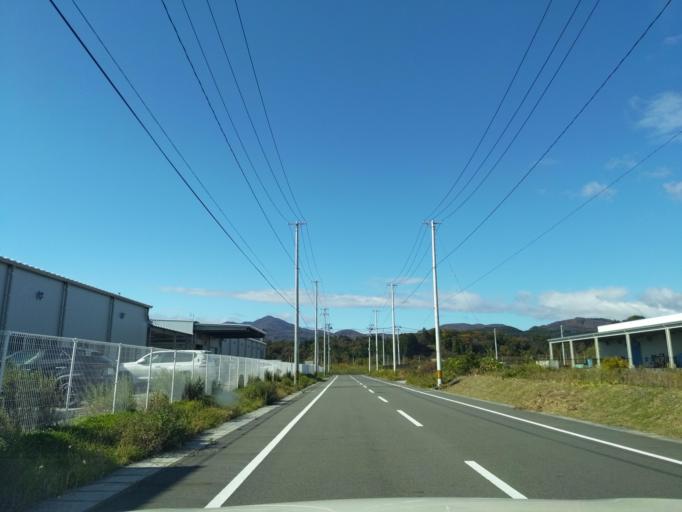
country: JP
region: Fukushima
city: Koriyama
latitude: 37.4624
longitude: 140.3037
